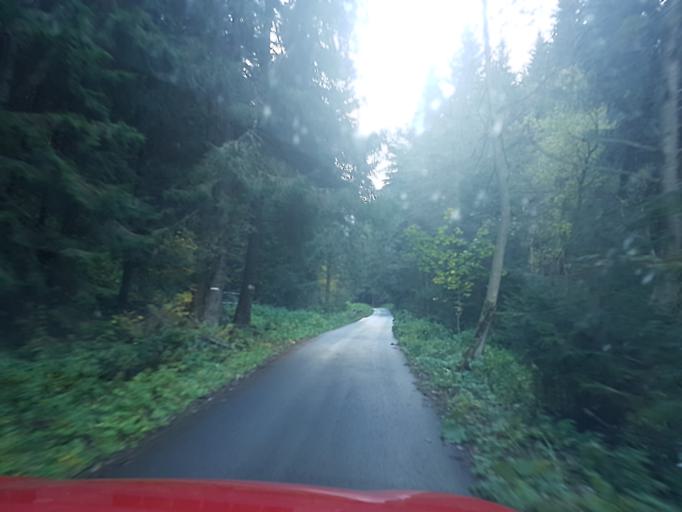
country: SK
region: Zilinsky
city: Ruzomberok
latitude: 48.9995
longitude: 19.2430
